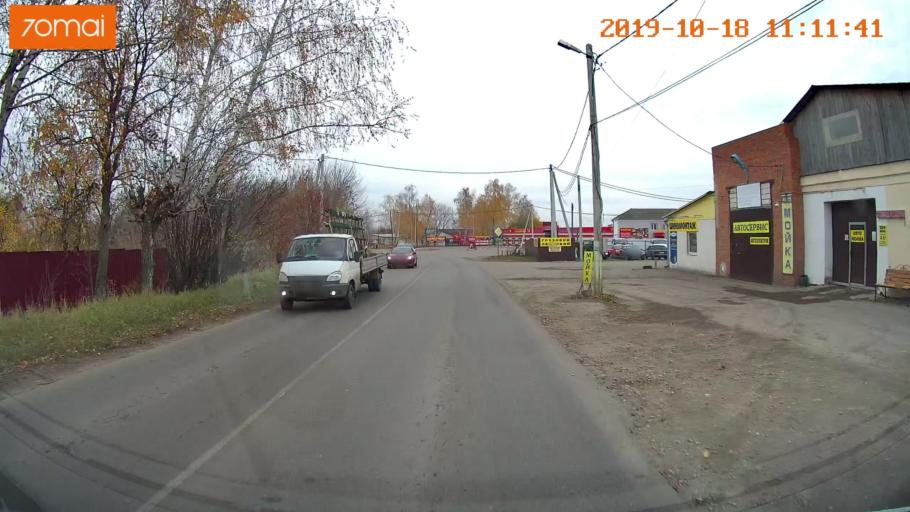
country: RU
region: Tula
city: Kimovsk
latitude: 53.9610
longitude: 38.5508
